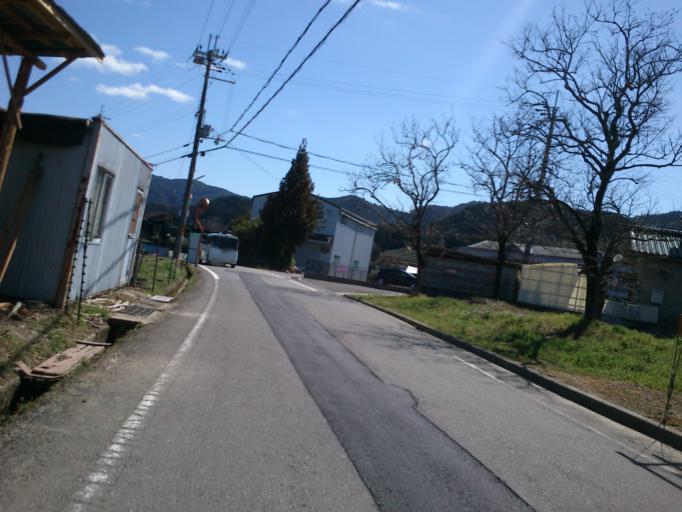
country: JP
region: Kyoto
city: Uji
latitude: 34.8393
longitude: 135.8576
